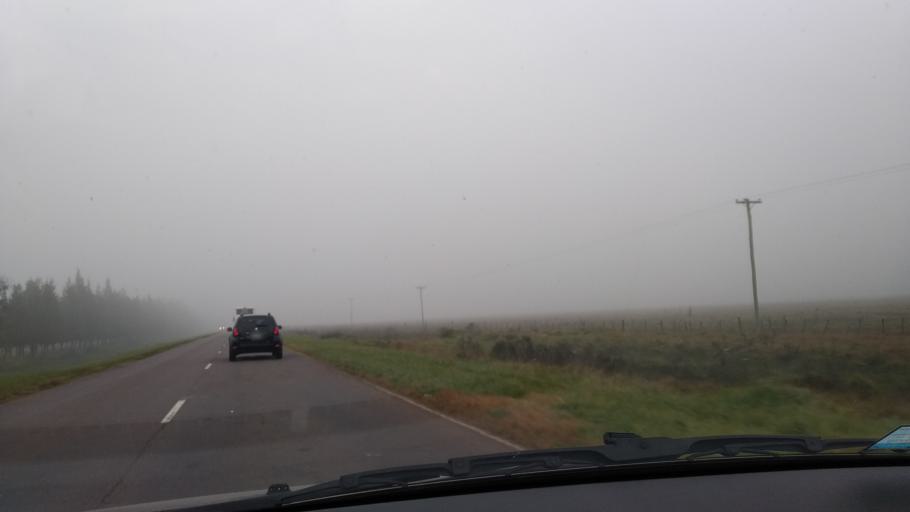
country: AR
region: Buenos Aires
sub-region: Partido de San Vicente
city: San Vicente
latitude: -35.2789
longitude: -58.5538
